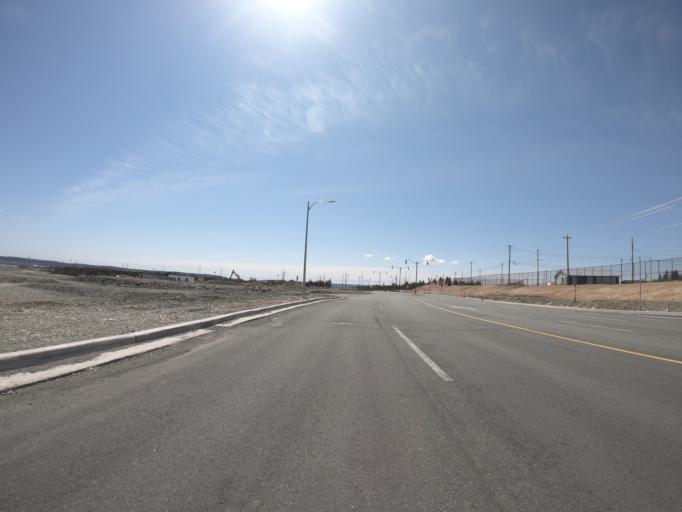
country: CA
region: Newfoundland and Labrador
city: Mount Pearl
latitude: 47.5075
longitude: -52.8293
